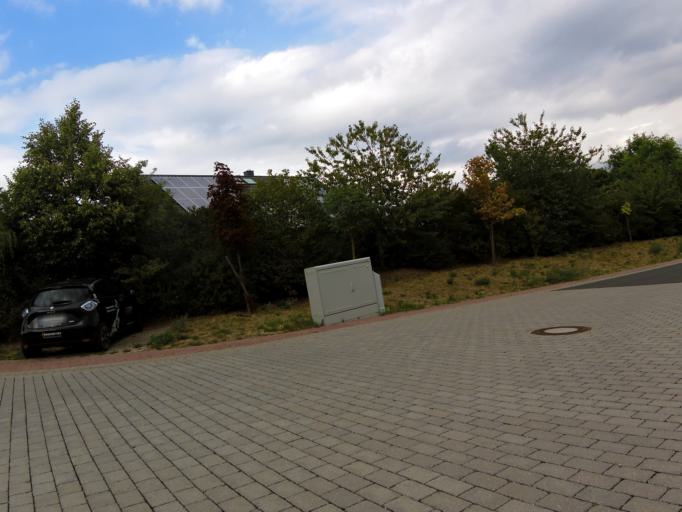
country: DE
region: Bavaria
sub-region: Regierungsbezirk Unterfranken
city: Hochberg
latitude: 49.7787
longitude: 9.8695
